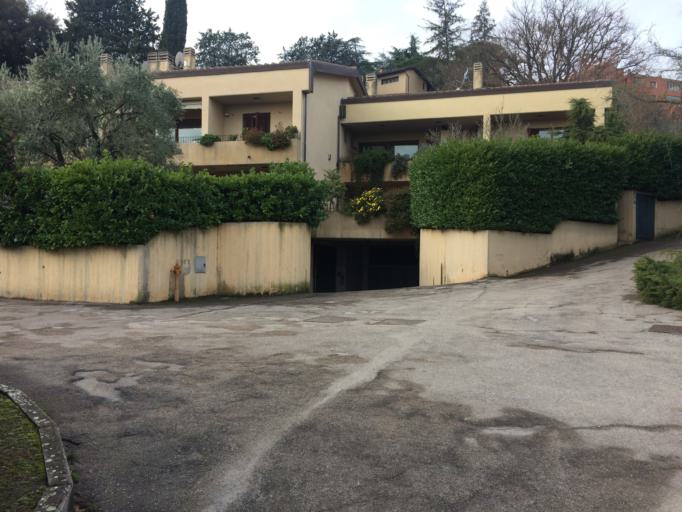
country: IT
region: Umbria
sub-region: Provincia di Perugia
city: Perugia
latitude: 43.0977
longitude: 12.4019
